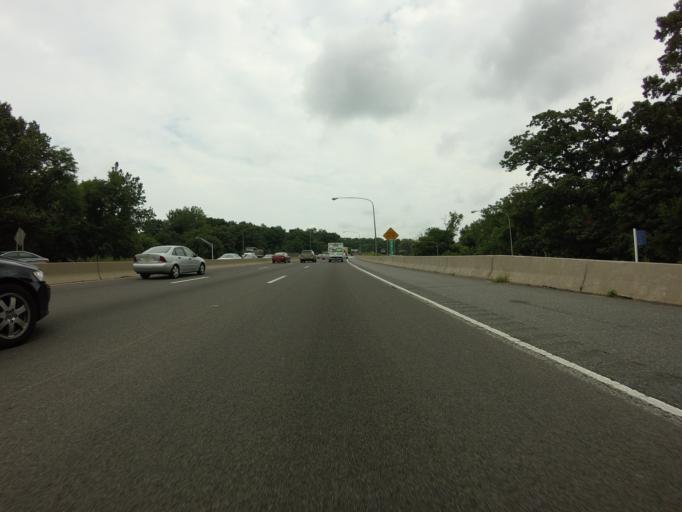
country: US
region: Pennsylvania
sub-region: Montgomery County
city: Bala-Cynwyd
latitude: 39.9857
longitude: -75.2081
